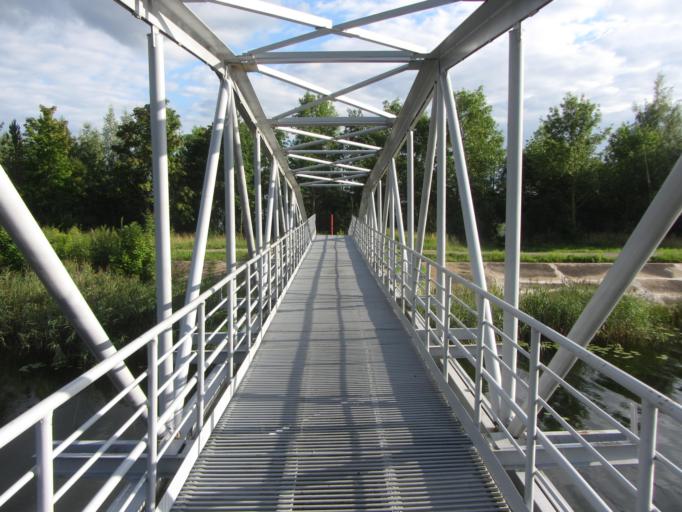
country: LT
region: Vilnius County
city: Elektrenai
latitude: 54.7729
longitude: 24.6527
